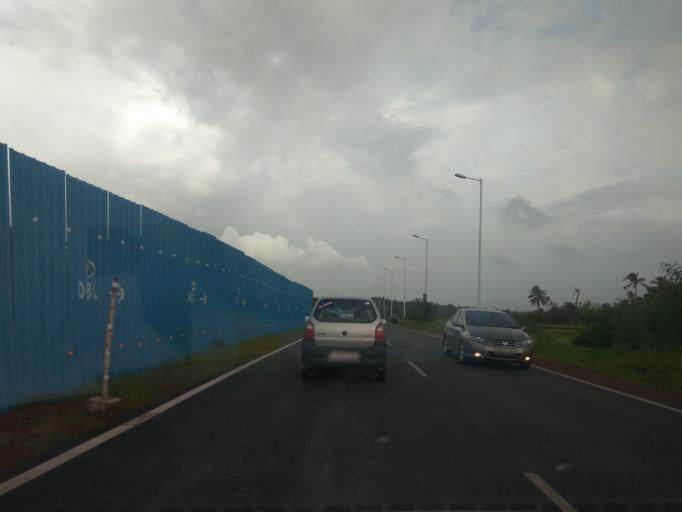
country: IN
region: Goa
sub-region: North Goa
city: Goa Velha
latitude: 15.4301
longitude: 73.8900
